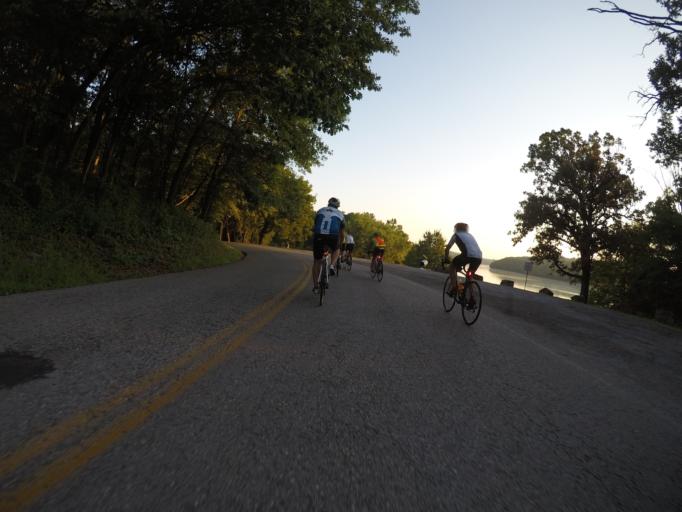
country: US
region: Kansas
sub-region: Wyandotte County
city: Edwardsville
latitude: 39.1536
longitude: -94.7903
